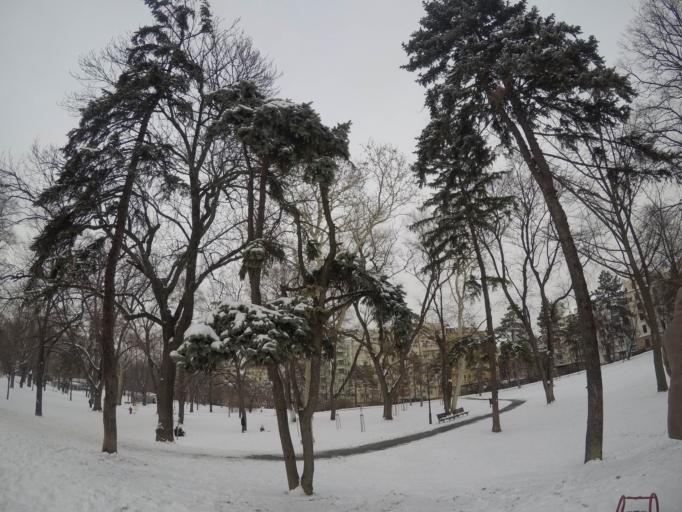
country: RS
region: Central Serbia
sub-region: Belgrade
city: Stari Grad
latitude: 44.8227
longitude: 20.4544
